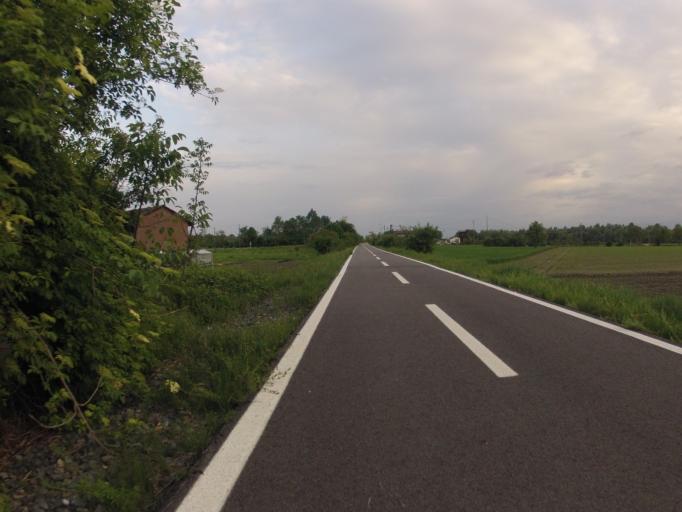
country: IT
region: Piedmont
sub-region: Provincia di Torino
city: Vigone
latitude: 44.8177
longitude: 7.4975
